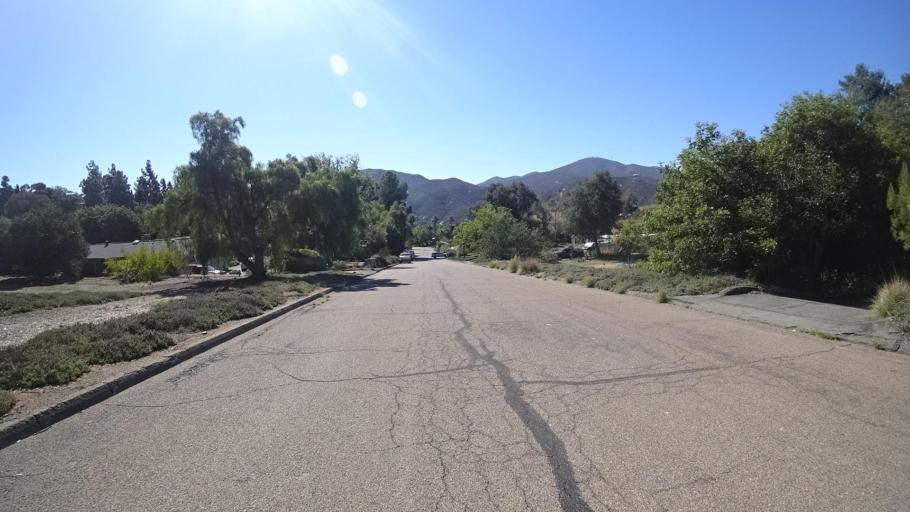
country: US
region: California
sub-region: San Diego County
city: Rancho San Diego
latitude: 32.7317
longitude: -116.9139
